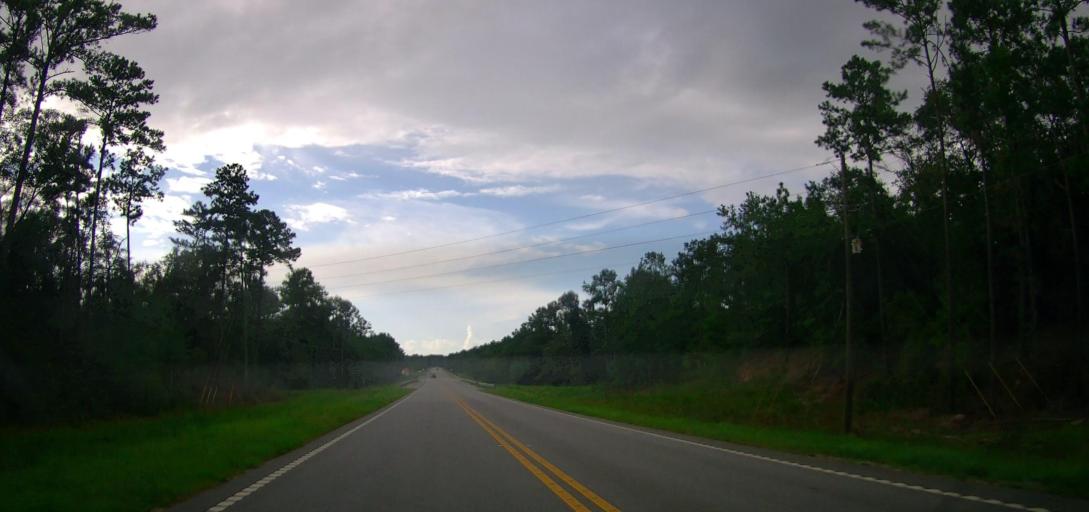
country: US
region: Georgia
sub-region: Ware County
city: Deenwood
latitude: 31.2956
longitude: -82.5562
